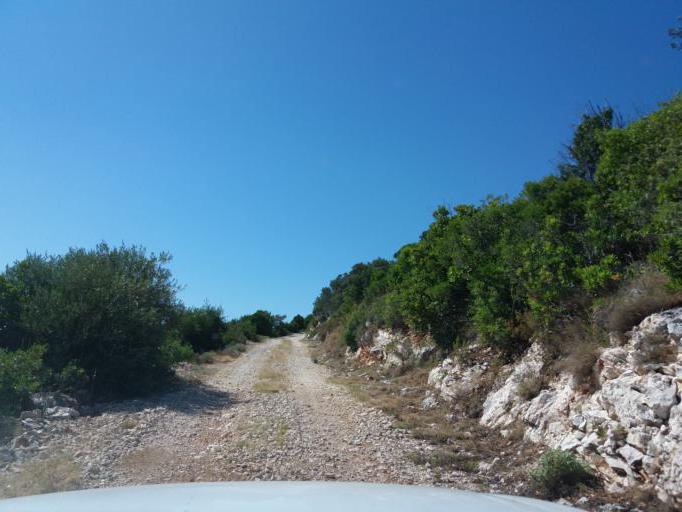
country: HR
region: Zadarska
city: Sali
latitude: 44.0047
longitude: 15.0374
